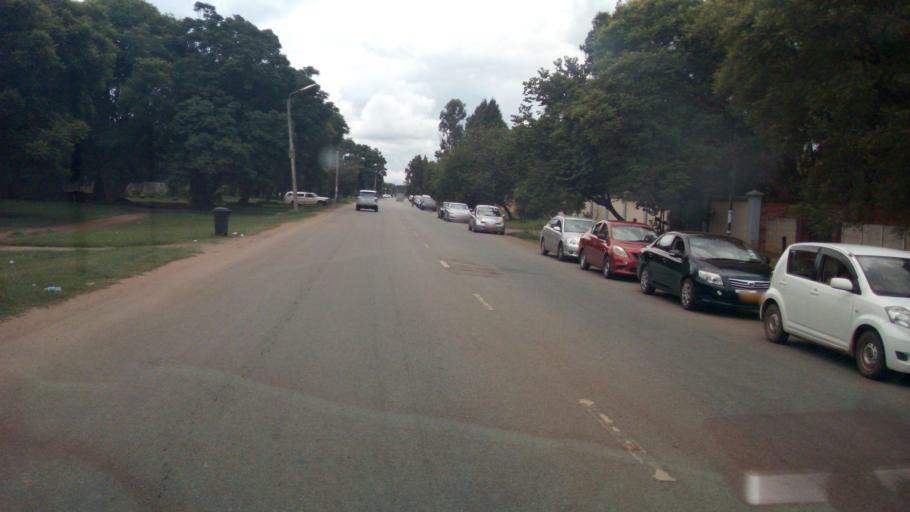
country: ZW
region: Harare
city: Harare
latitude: -17.7513
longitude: 31.0162
